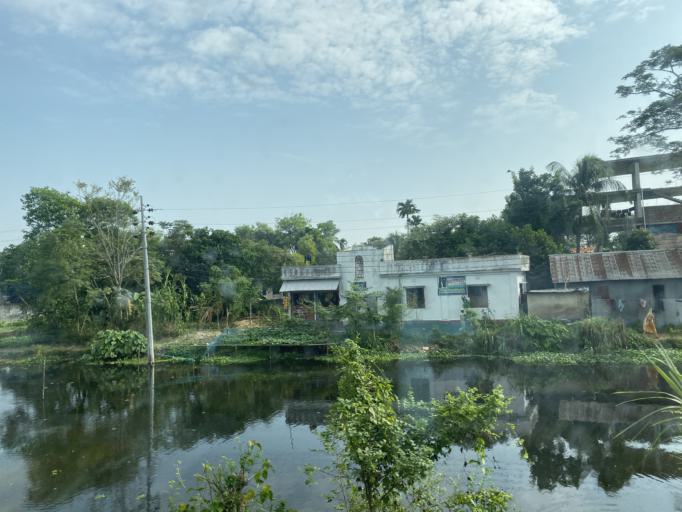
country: BD
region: Chittagong
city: Nabinagar
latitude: 23.9466
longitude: 91.1204
